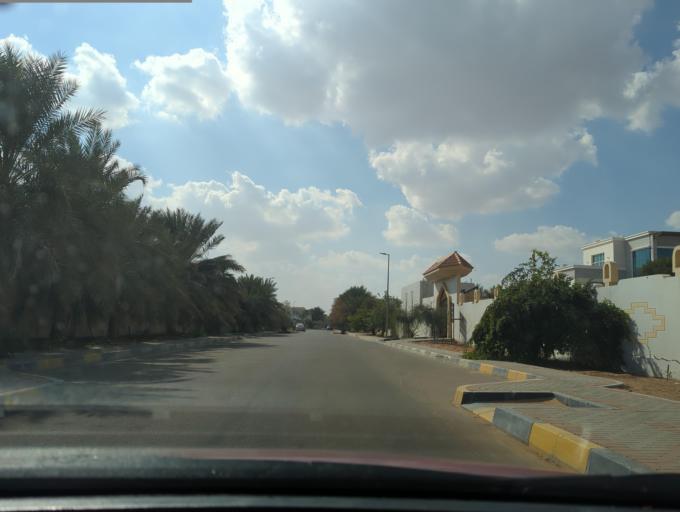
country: AE
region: Abu Dhabi
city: Al Ain
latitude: 24.1540
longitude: 55.6566
